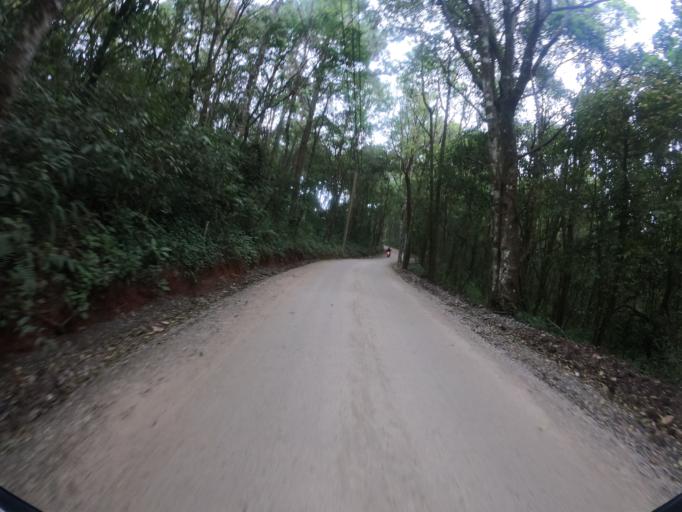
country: TH
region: Chiang Mai
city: Chiang Mai
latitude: 18.8171
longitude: 98.8908
